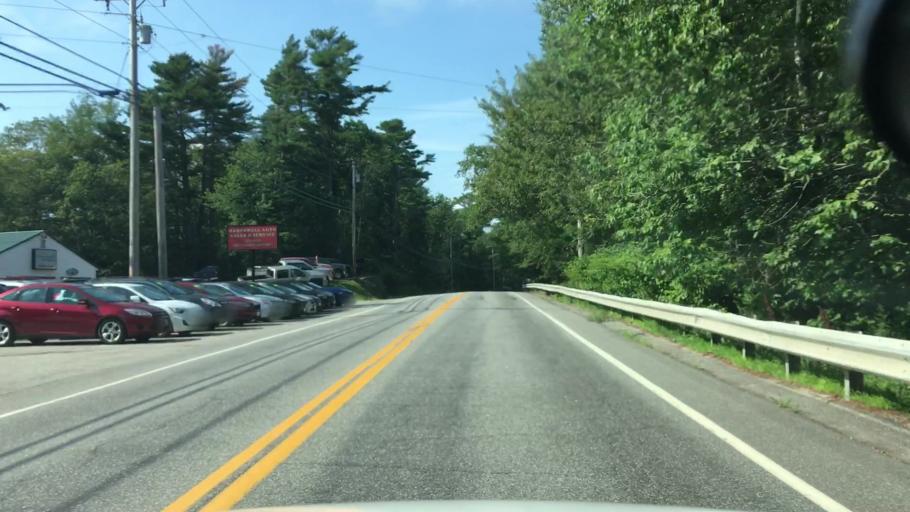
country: US
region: Maine
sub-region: Cumberland County
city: Harpswell Center
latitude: 43.8407
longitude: -69.9124
